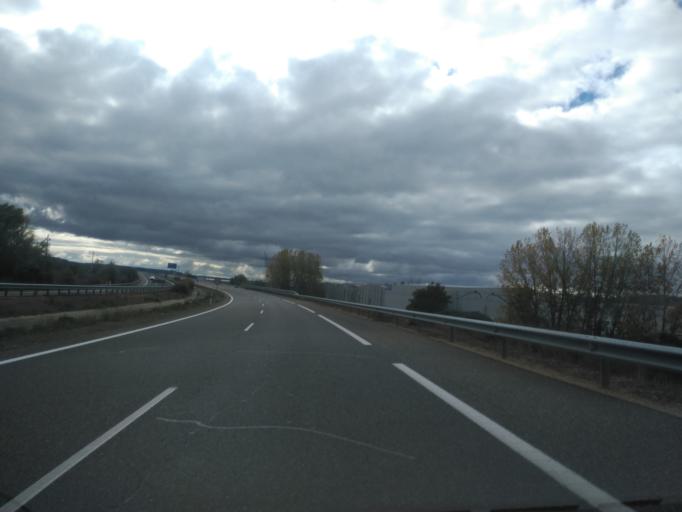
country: ES
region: Castille and Leon
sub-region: Provincia de Palencia
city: Villamuriel de Cerrato
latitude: 41.9667
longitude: -4.5049
